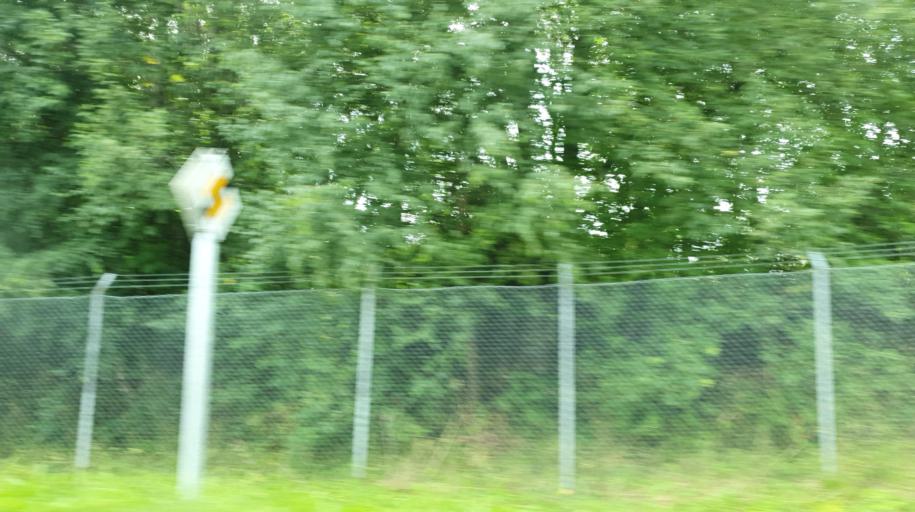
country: NO
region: Nord-Trondelag
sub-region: Stjordal
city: Stjordalshalsen
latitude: 63.4632
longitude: 10.9431
